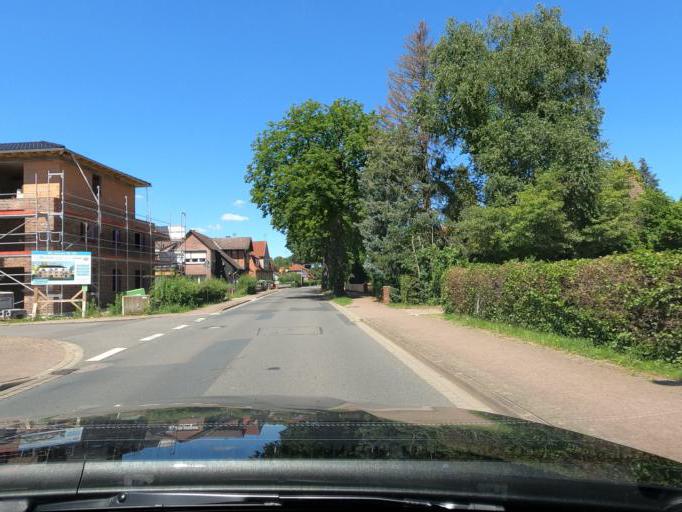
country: DE
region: Lower Saxony
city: Wienhausen
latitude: 52.5764
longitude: 10.1859
